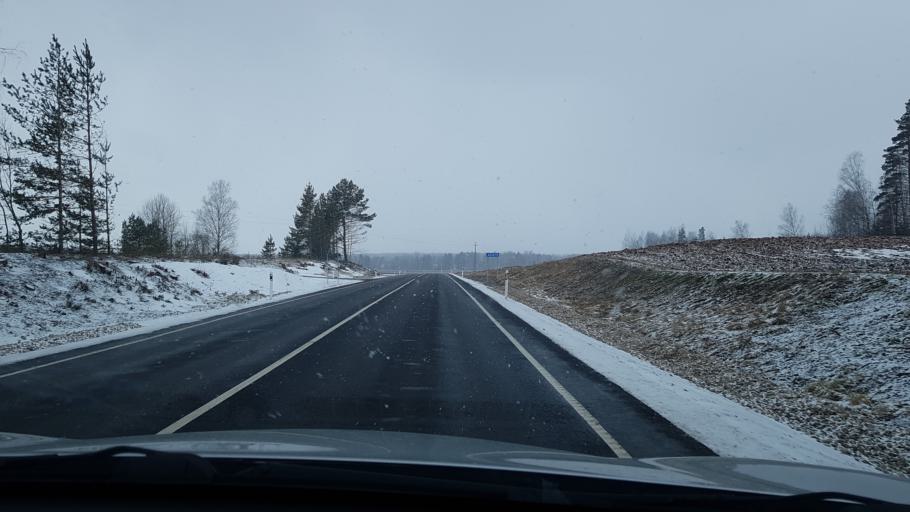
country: EE
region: Polvamaa
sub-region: Polva linn
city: Polva
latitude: 58.0950
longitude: 27.1569
